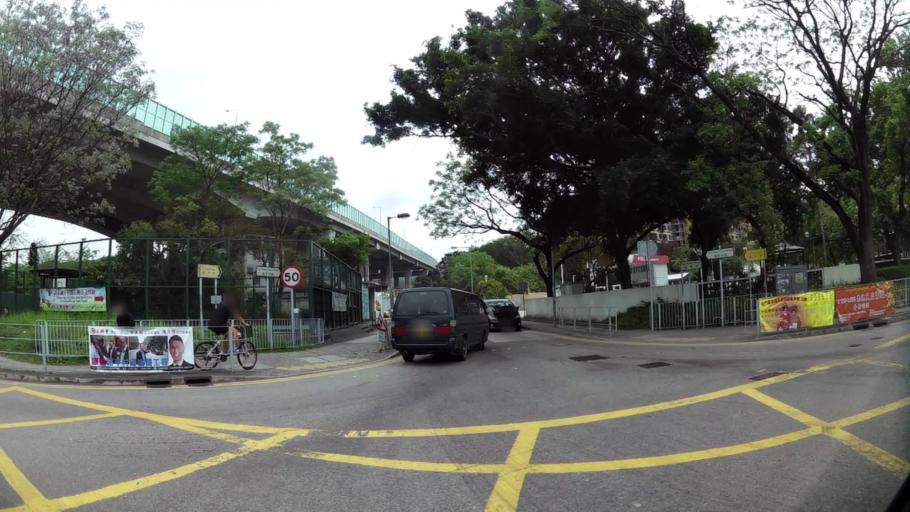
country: HK
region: Tuen Mun
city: Tuen Mun
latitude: 22.4215
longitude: 113.9848
